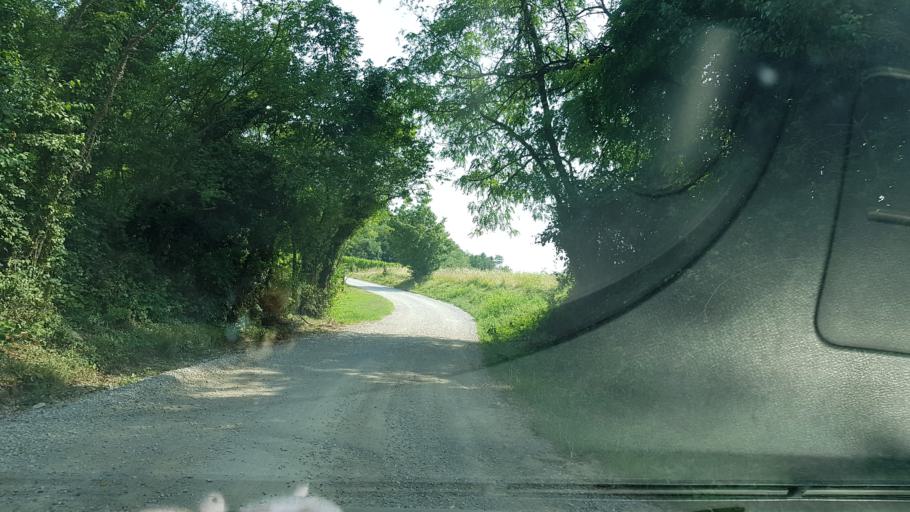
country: SI
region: Brda
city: Dobrovo
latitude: 45.9947
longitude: 13.5165
